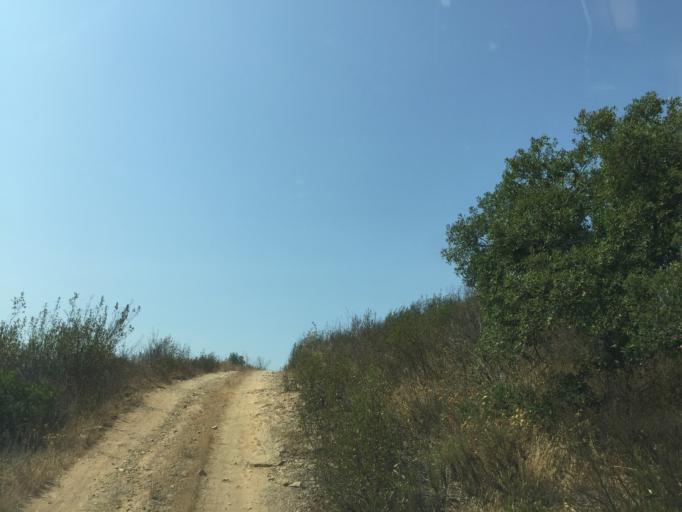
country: PT
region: Setubal
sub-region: Santiago do Cacem
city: Santiago do Cacem
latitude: 37.9743
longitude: -8.5173
